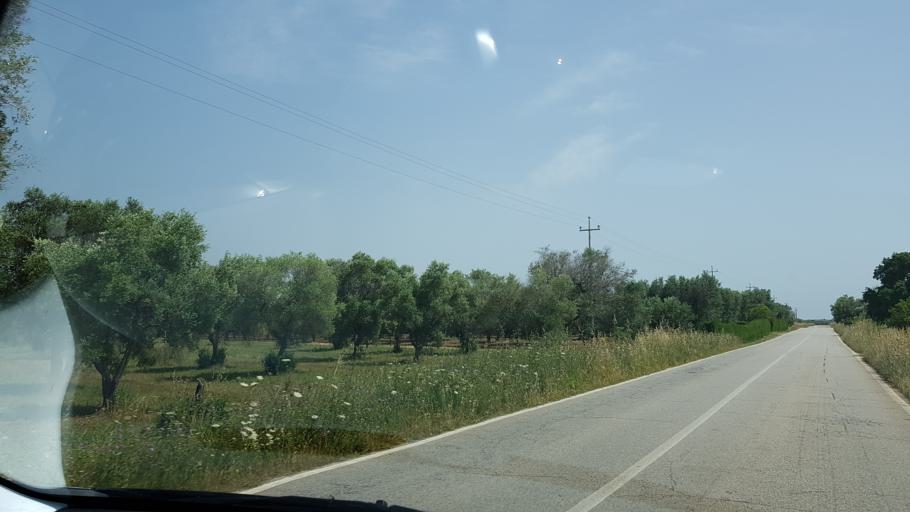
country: IT
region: Apulia
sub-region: Provincia di Brindisi
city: San Pancrazio Salentino
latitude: 40.4523
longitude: 17.8406
